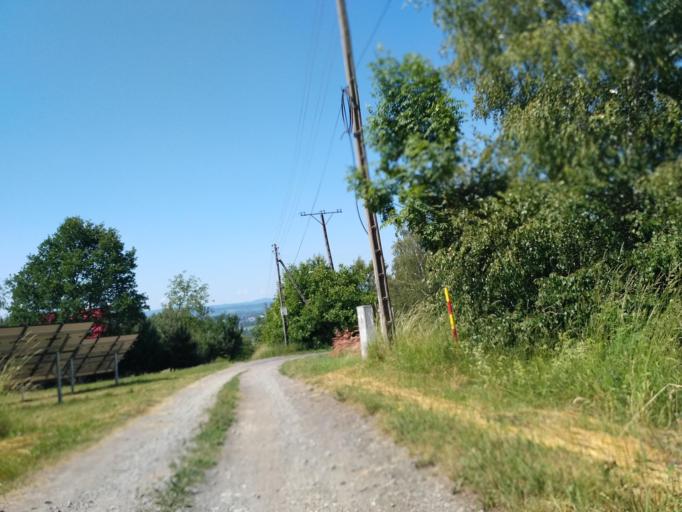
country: PL
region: Subcarpathian Voivodeship
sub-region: Powiat krosnienski
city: Korczyna
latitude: 49.7329
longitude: 21.7826
